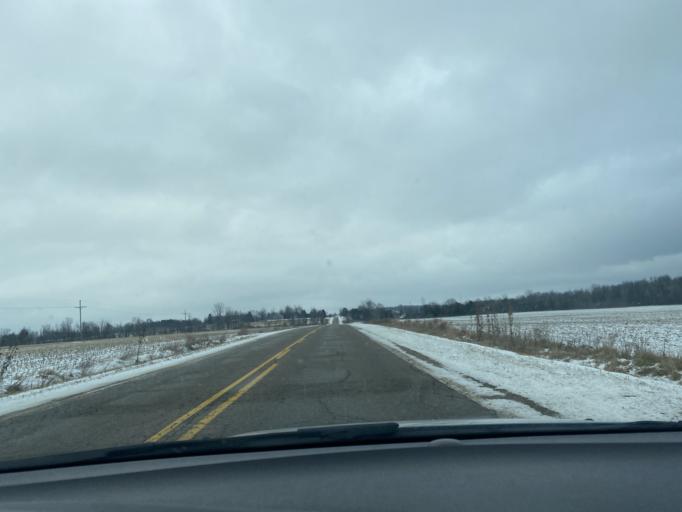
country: US
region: Michigan
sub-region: Lapeer County
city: North Branch
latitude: 43.2083
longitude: -83.1710
